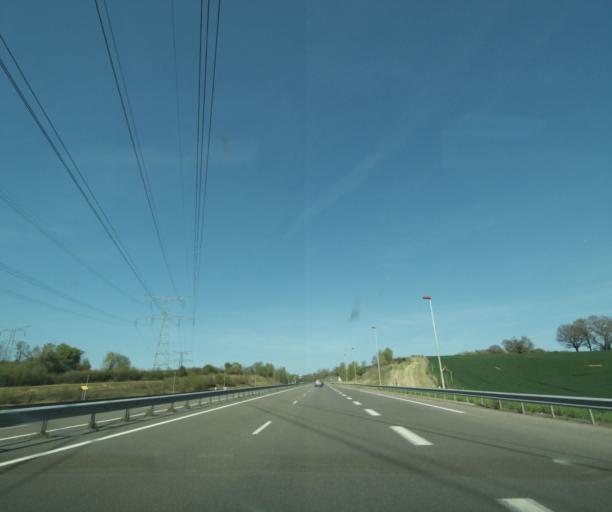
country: FR
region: Bourgogne
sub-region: Departement de la Nievre
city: Coulanges-les-Nevers
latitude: 47.0127
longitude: 3.2014
